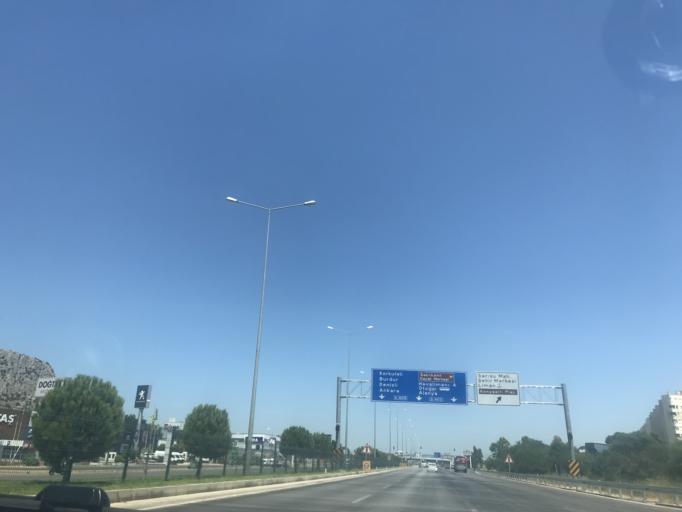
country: TR
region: Antalya
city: Cakirlar
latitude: 36.8413
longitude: 30.5975
